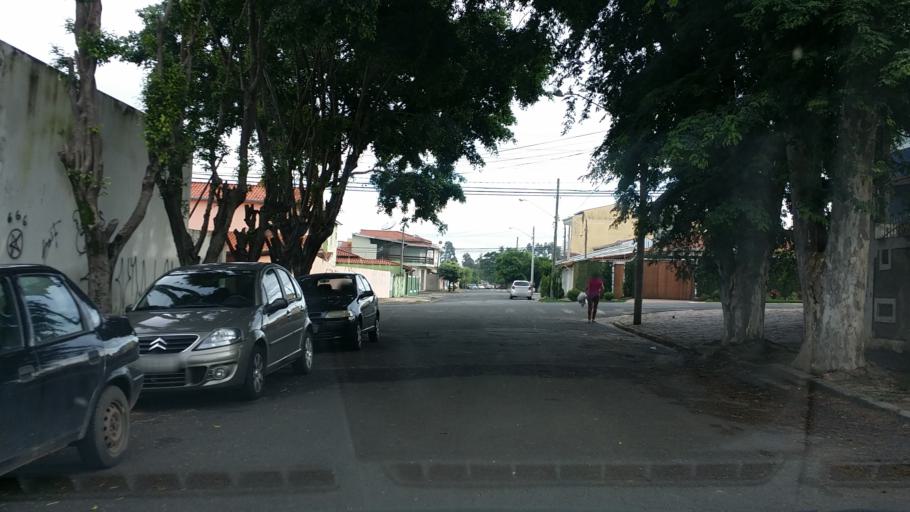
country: BR
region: Sao Paulo
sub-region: Indaiatuba
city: Indaiatuba
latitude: -23.1146
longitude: -47.2256
